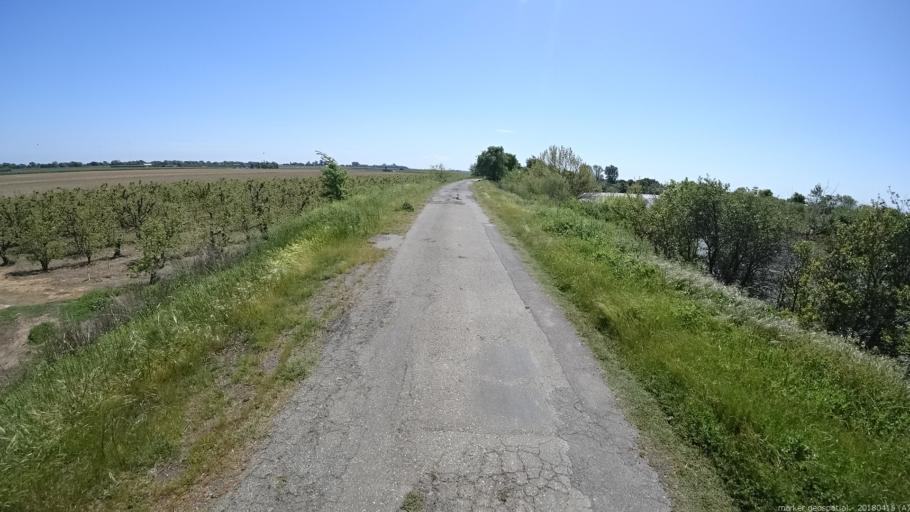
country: US
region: California
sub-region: Sacramento County
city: Walnut Grove
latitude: 38.3030
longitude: -121.5993
